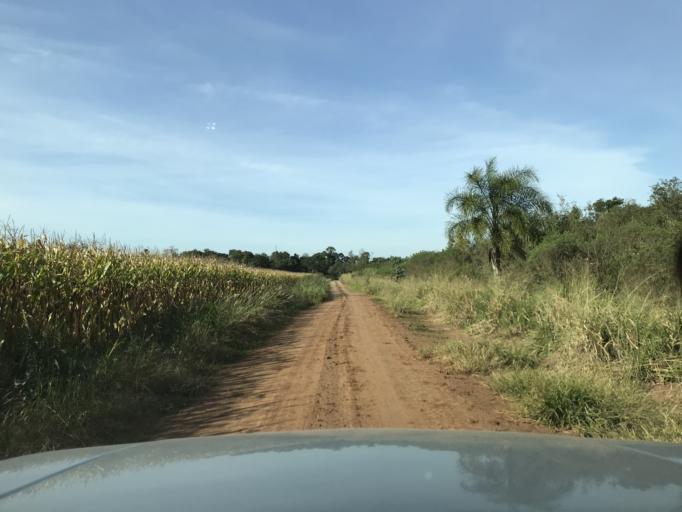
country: BR
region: Parana
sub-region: Palotina
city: Palotina
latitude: -24.2514
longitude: -53.7546
